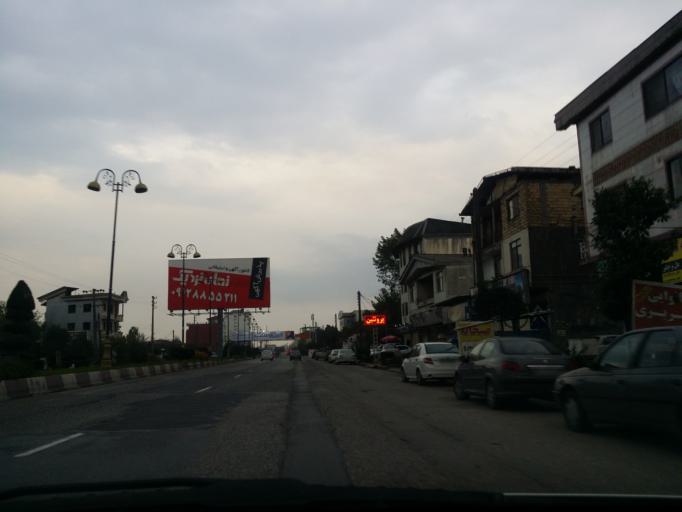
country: IR
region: Mazandaran
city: `Abbasabad
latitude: 36.7258
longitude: 51.1187
